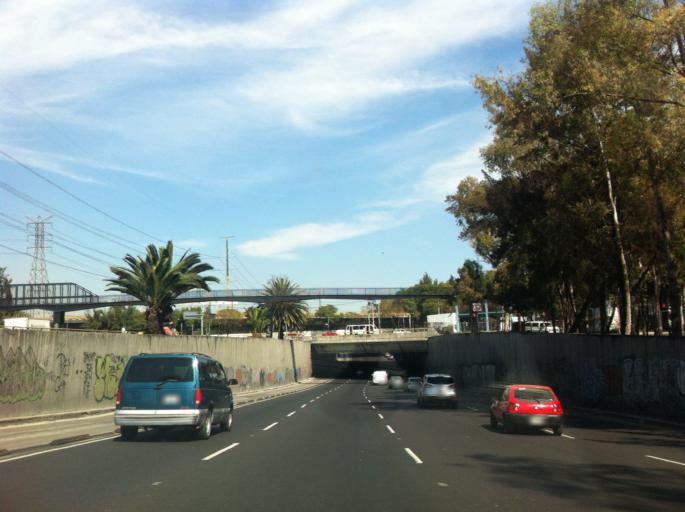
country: MX
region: Mexico
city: Colonia Lindavista
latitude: 19.4697
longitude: -99.1381
